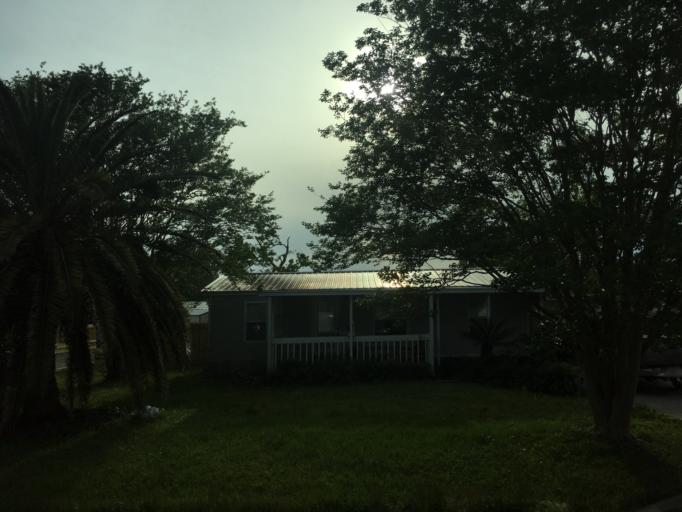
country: US
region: Florida
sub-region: Bay County
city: Upper Grand Lagoon
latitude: 30.1662
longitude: -85.7656
